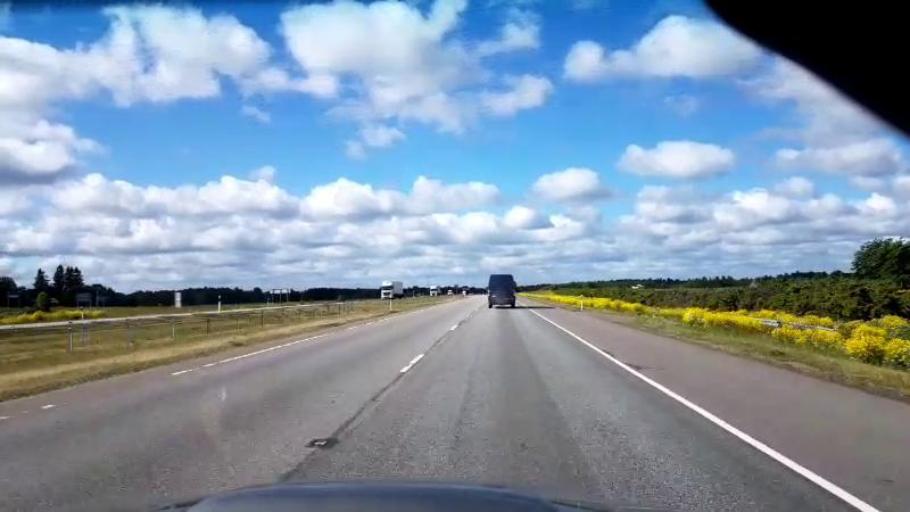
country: EE
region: Harju
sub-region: Saue linn
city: Saue
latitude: 59.3010
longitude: 24.5571
